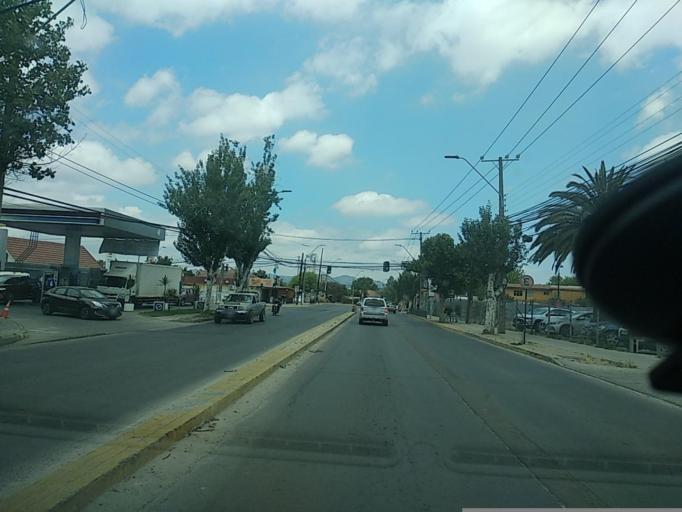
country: CL
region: Valparaiso
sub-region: Provincia de Marga Marga
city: Villa Alemana
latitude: -33.0455
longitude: -71.3902
